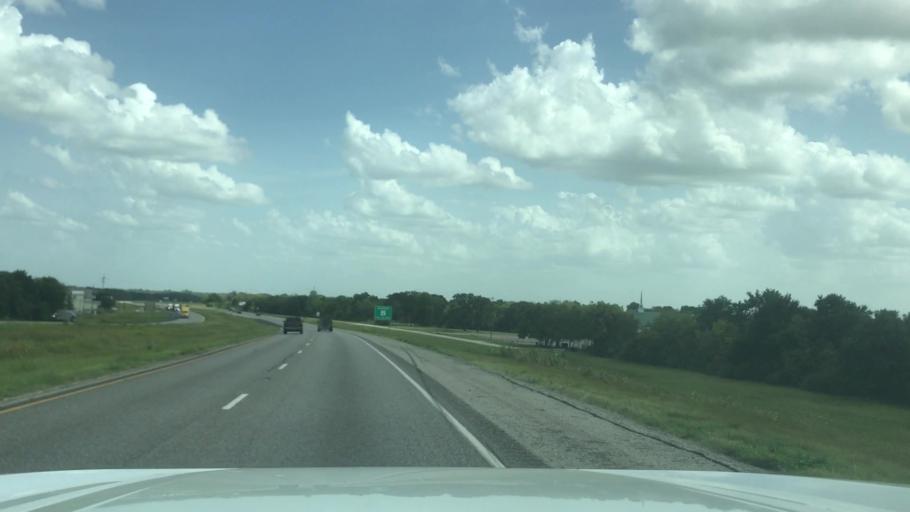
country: US
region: Texas
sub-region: Grimes County
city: Navasota
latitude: 30.3599
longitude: -96.0626
